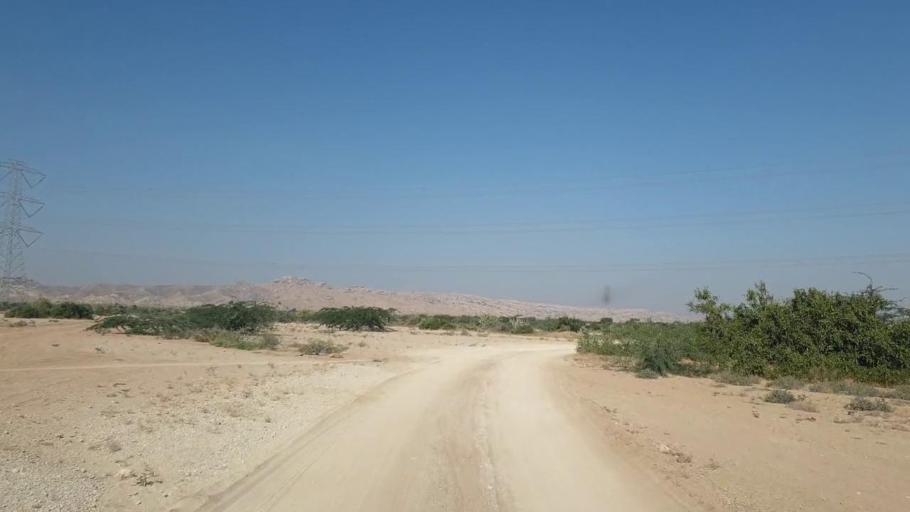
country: PK
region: Sindh
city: Gharo
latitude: 25.1954
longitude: 67.7422
